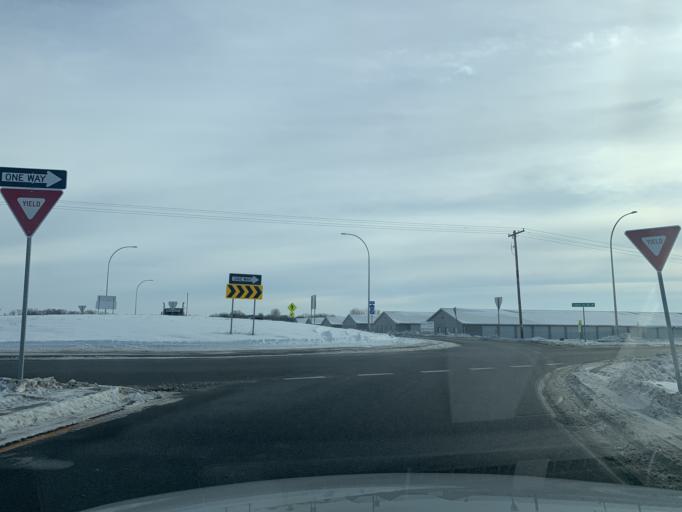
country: US
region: Minnesota
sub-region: Wright County
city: Buffalo
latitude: 45.1657
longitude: -93.8479
